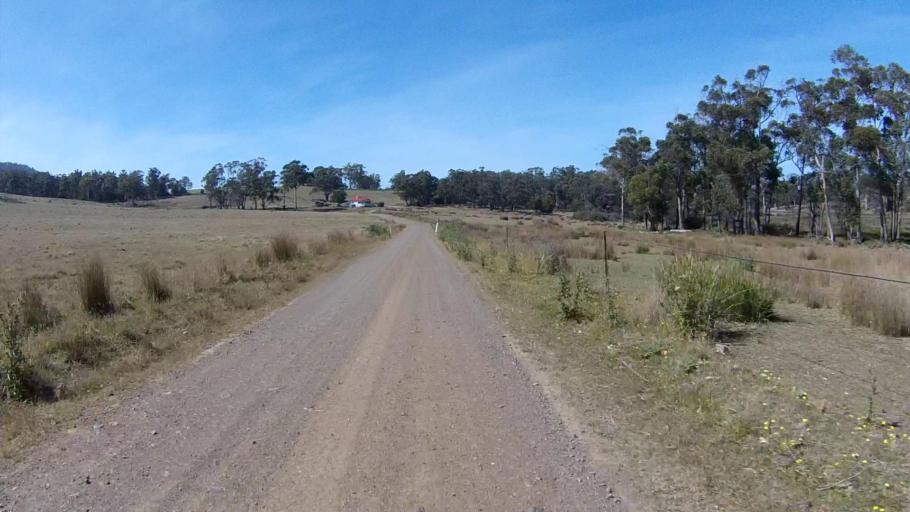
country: AU
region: Tasmania
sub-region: Sorell
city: Sorell
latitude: -42.7151
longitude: 147.5946
